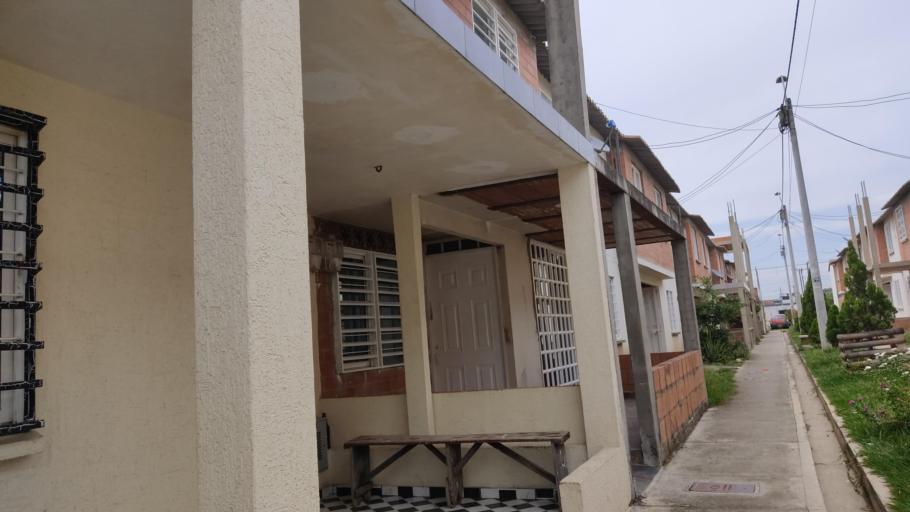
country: CO
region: Valle del Cauca
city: Jamundi
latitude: 3.2367
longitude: -76.5108
